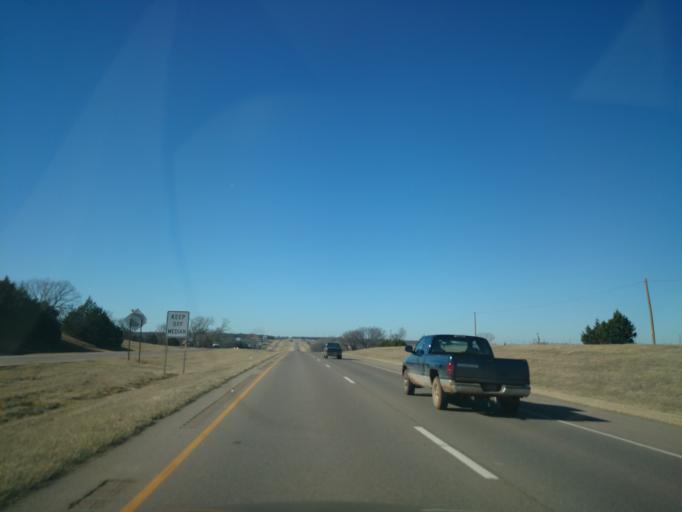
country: US
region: Oklahoma
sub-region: Payne County
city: Stillwater
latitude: 36.1161
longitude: -97.1467
